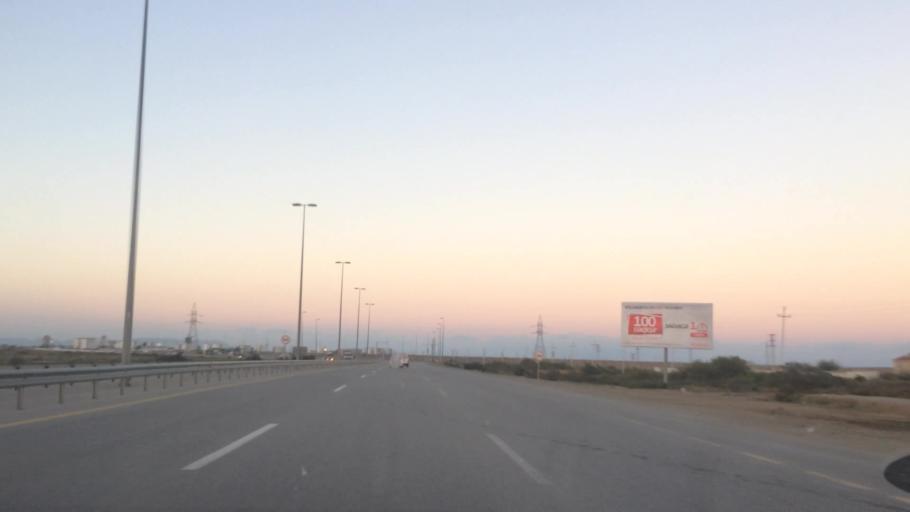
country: AZ
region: Baki
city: Qobustan
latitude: 39.9879
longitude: 49.4286
